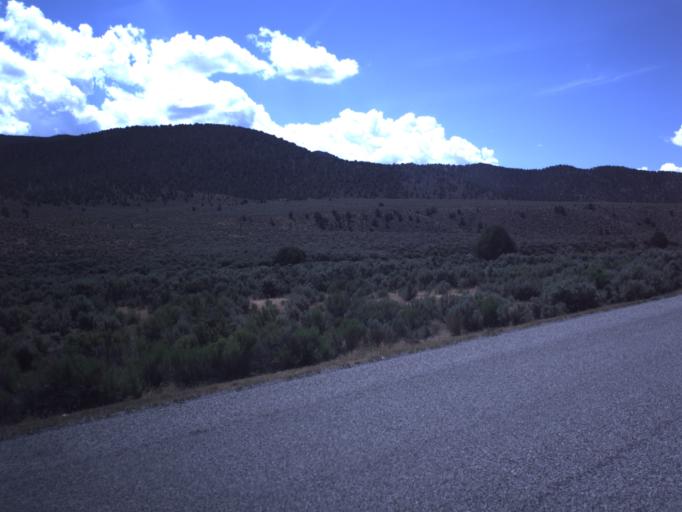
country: US
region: Utah
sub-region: Piute County
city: Junction
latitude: 38.0610
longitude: -112.3485
